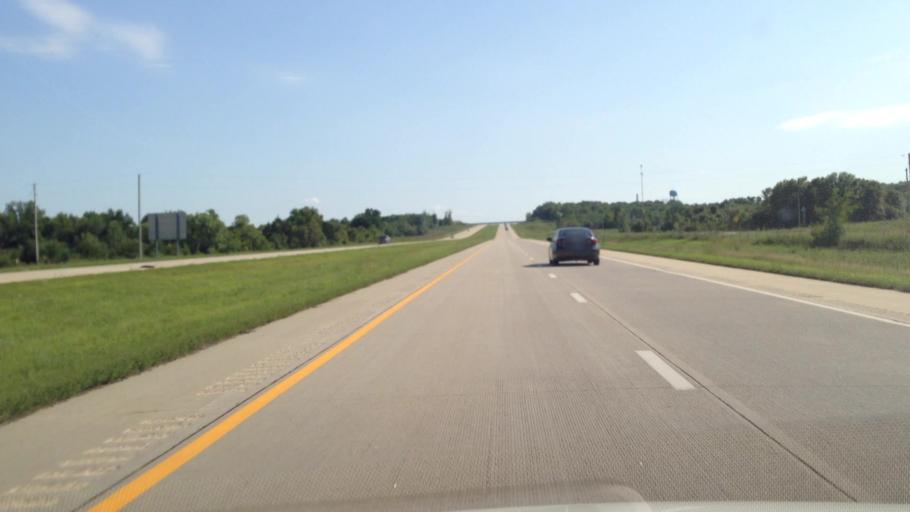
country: US
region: Kansas
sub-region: Linn County
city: Pleasanton
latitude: 38.1264
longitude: -94.7151
